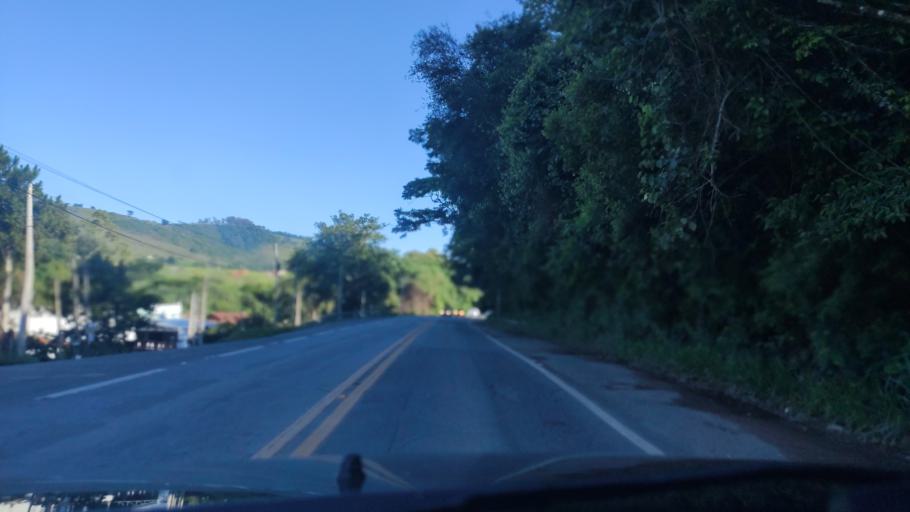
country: BR
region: Sao Paulo
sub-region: Socorro
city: Socorro
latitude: -22.6297
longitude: -46.5341
